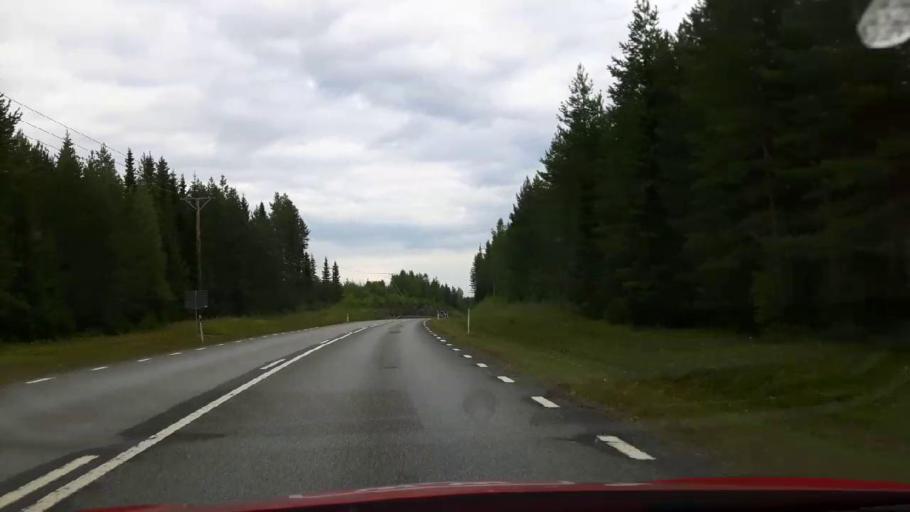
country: SE
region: Jaemtland
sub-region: Stroemsunds Kommun
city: Stroemsund
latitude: 63.6351
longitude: 15.3583
